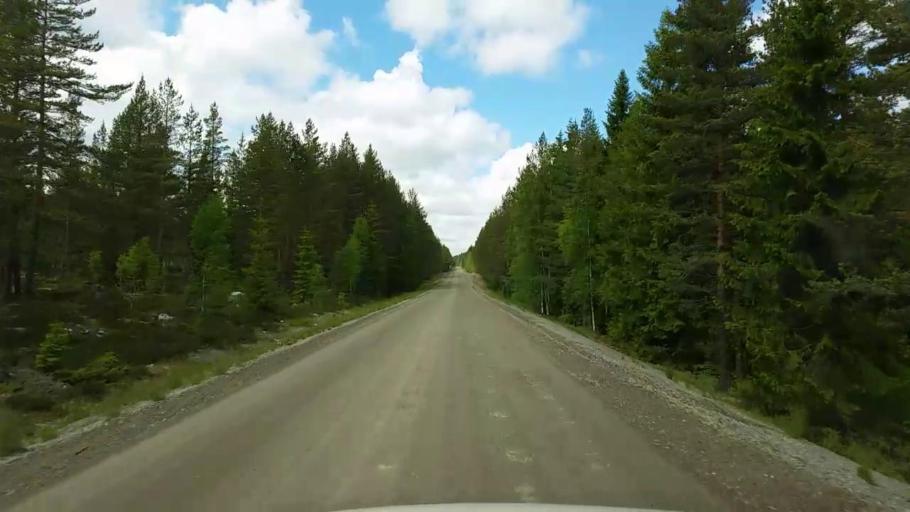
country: SE
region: Gaevleborg
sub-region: Bollnas Kommun
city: Vittsjo
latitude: 61.0331
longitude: 16.3688
